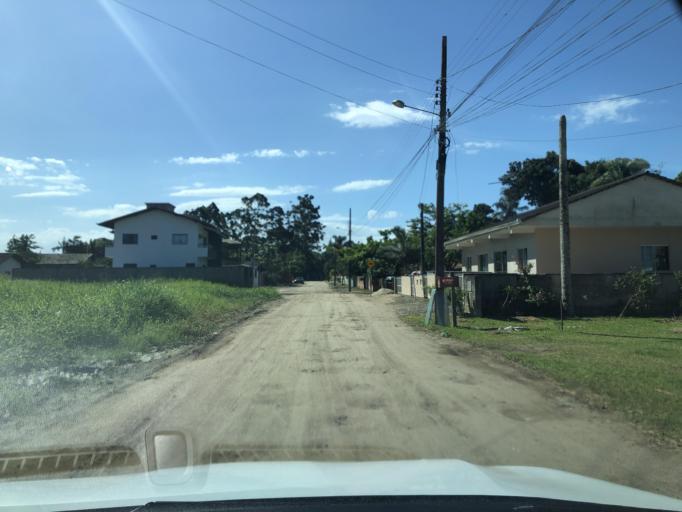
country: BR
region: Santa Catarina
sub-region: Sao Francisco Do Sul
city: Sao Francisco do Sul
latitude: -26.2087
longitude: -48.5364
